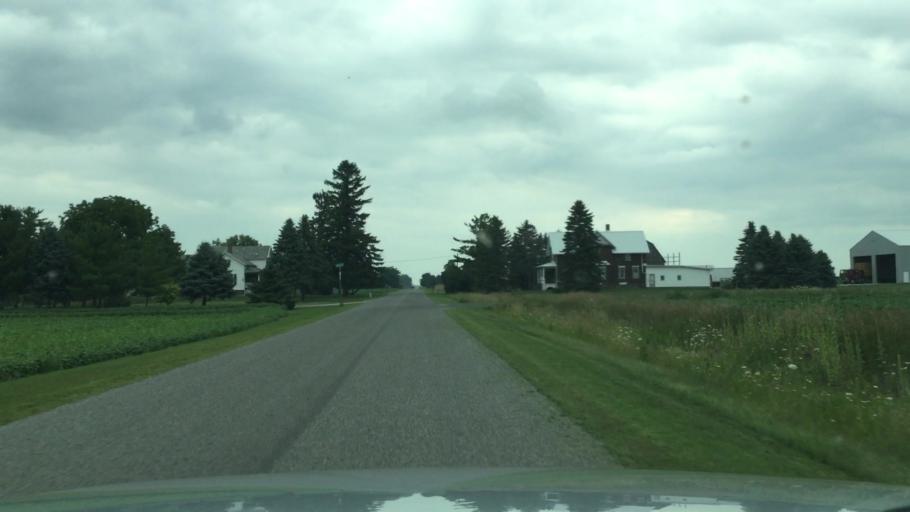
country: US
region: Michigan
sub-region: Saginaw County
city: Frankenmuth
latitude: 43.3424
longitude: -83.7786
